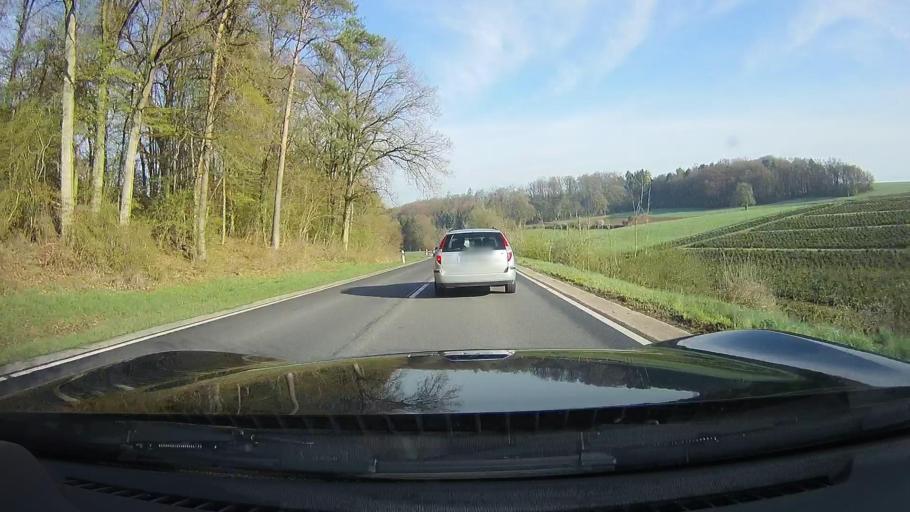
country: DE
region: Baden-Wuerttemberg
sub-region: Karlsruhe Region
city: Billigheim
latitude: 49.4091
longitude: 9.2456
